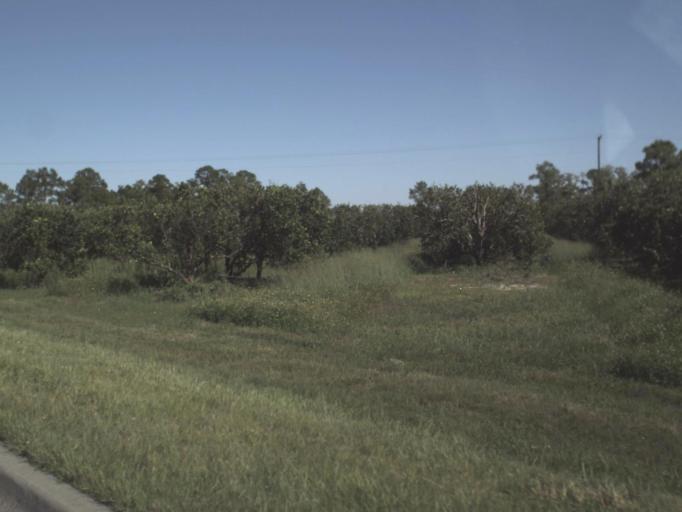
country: US
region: Florida
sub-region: Hendry County
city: LaBelle
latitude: 26.7422
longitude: -81.4650
